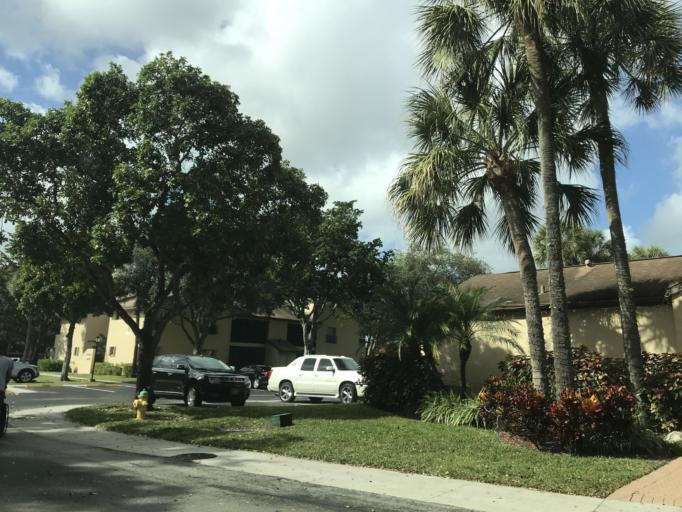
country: US
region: Florida
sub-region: Broward County
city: Coconut Creek
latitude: 26.2693
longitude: -80.1902
